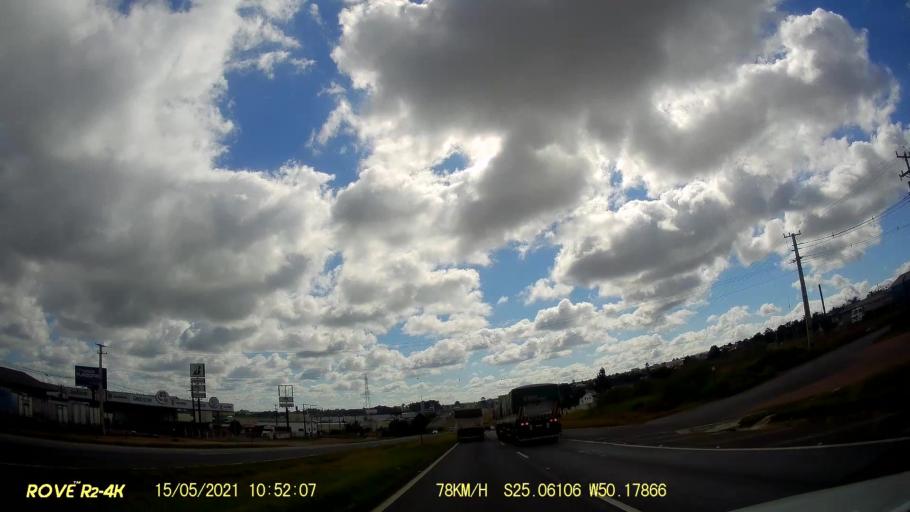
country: BR
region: Parana
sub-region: Ponta Grossa
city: Ponta Grossa
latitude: -25.0613
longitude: -50.1787
